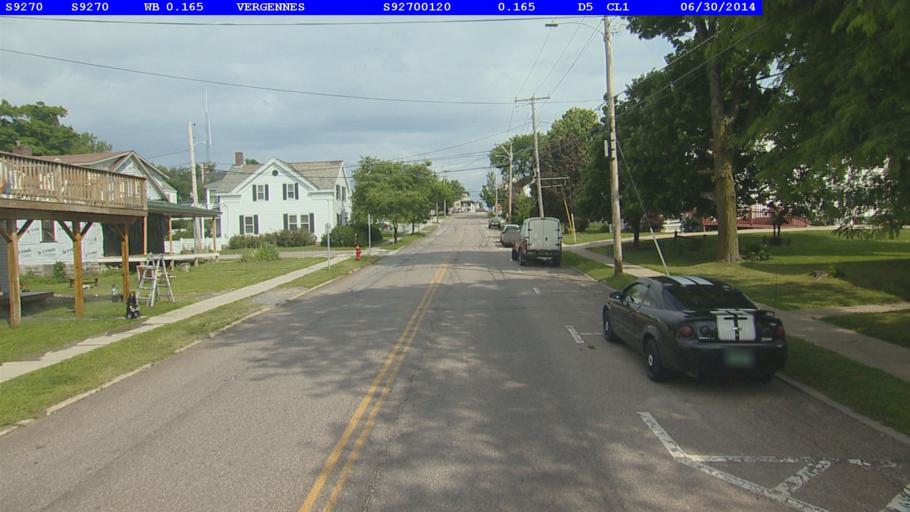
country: US
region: Vermont
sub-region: Addison County
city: Vergennes
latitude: 44.1659
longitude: -73.2500
